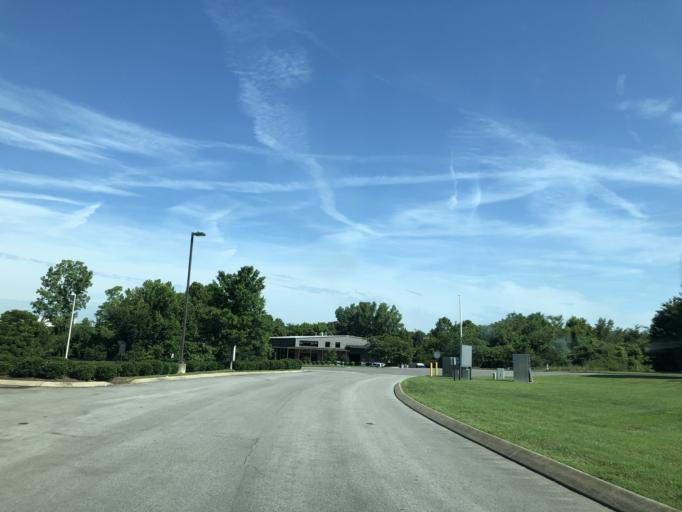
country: US
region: Tennessee
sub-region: Rutherford County
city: La Vergne
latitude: 36.0356
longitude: -86.6321
